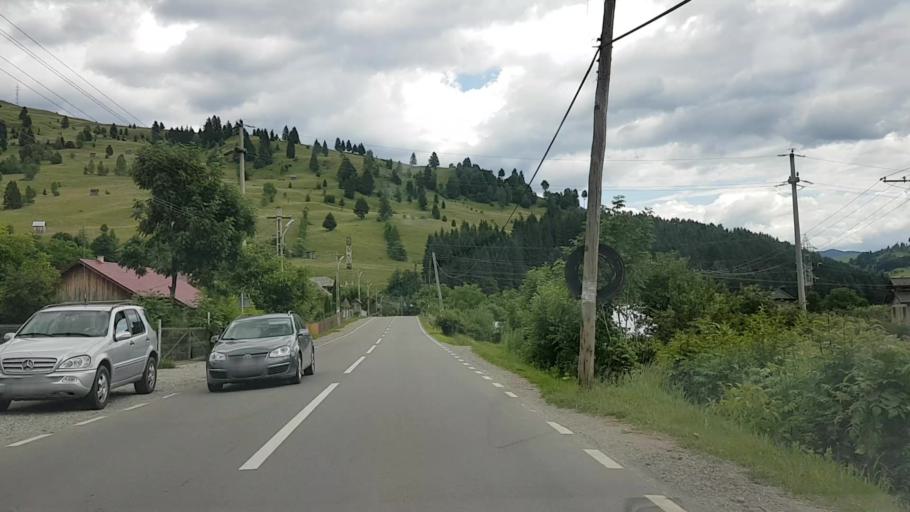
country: RO
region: Neamt
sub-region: Comuna Borca
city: Borca
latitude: 47.1786
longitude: 25.7874
